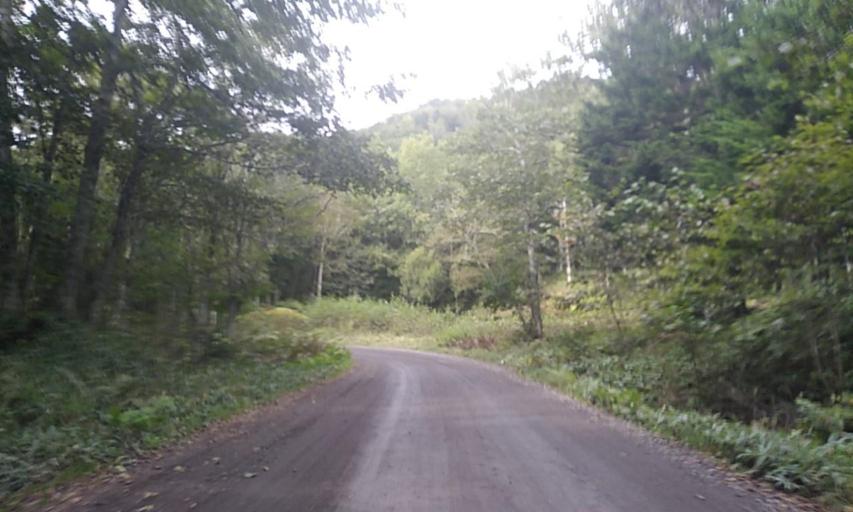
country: JP
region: Hokkaido
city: Abashiri
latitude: 43.6575
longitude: 144.5498
